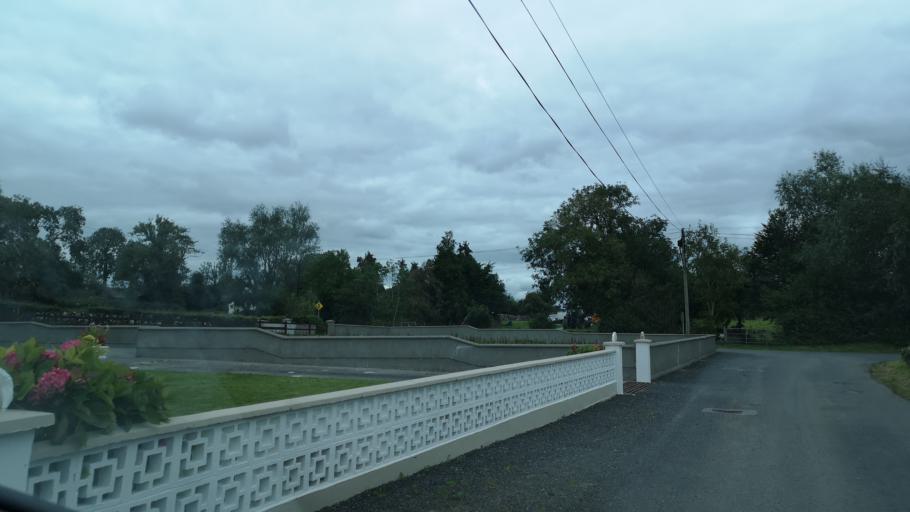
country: IE
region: Connaught
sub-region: County Galway
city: Loughrea
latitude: 53.1584
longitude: -8.4340
